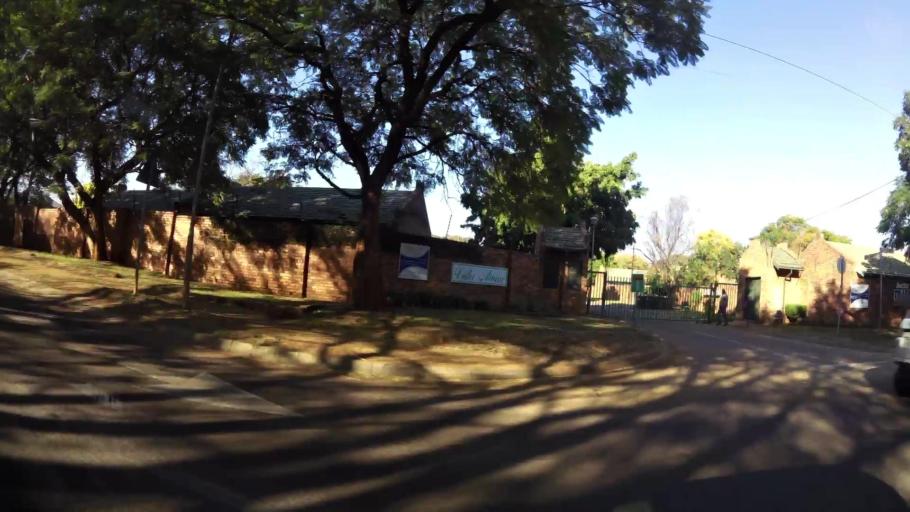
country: ZA
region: Gauteng
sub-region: City of Tshwane Metropolitan Municipality
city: Pretoria
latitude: -25.6707
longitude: 28.1986
